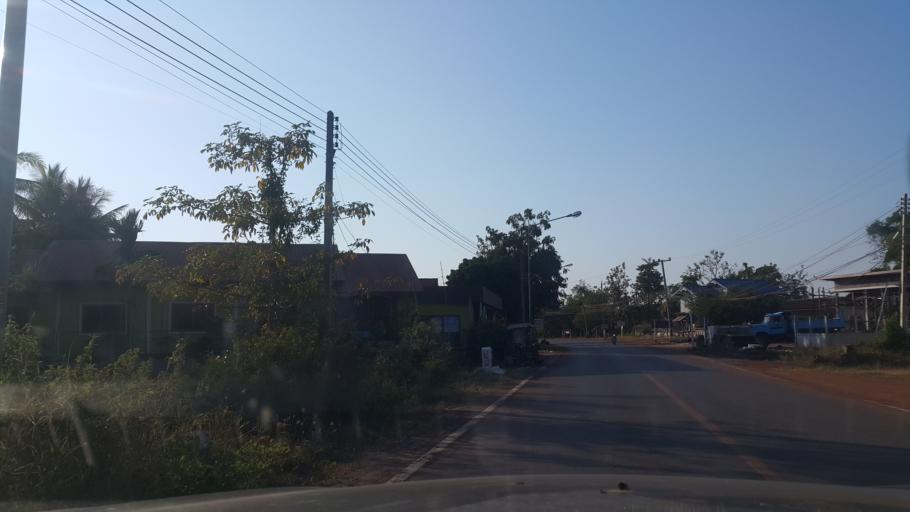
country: TH
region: Changwat Udon Thani
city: Ban Na Muang
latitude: 17.2323
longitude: 103.0431
